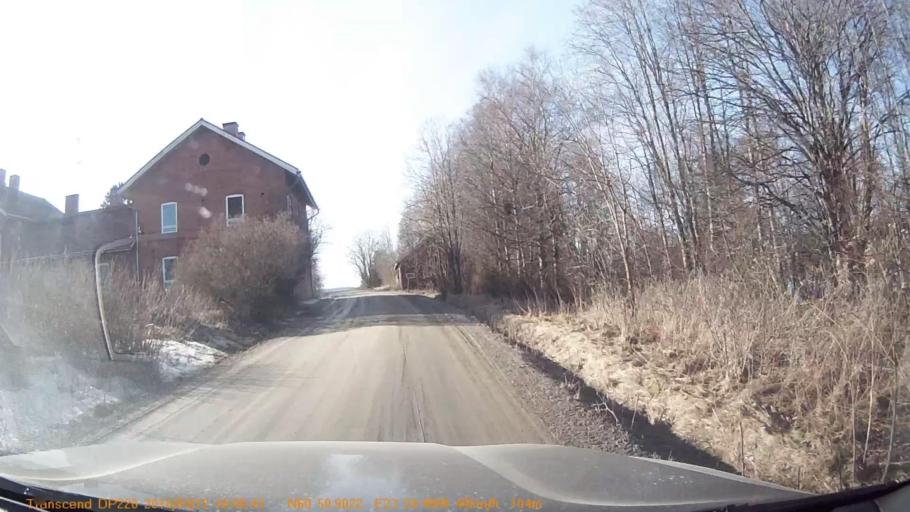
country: FI
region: Haeme
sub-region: Forssa
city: Jokioinen
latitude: 60.8485
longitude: 23.4745
